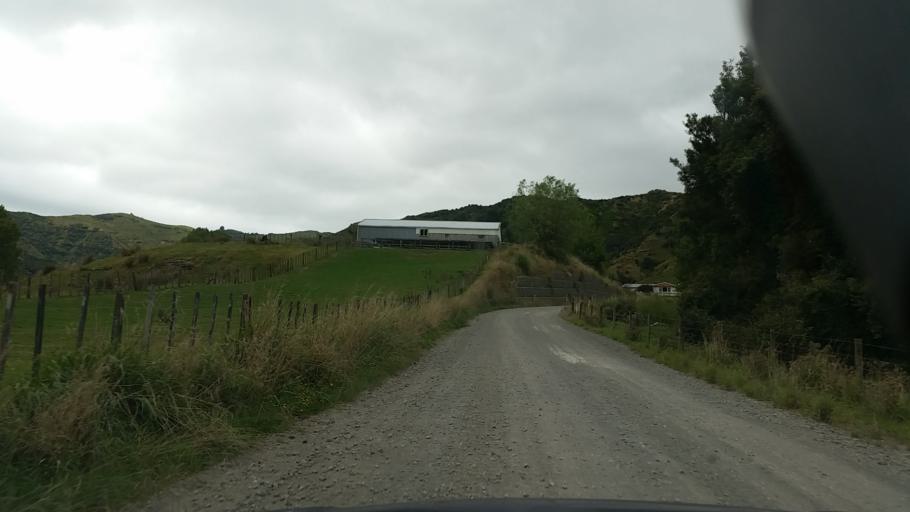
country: NZ
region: Taranaki
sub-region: South Taranaki District
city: Eltham
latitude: -39.3425
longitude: 174.5741
